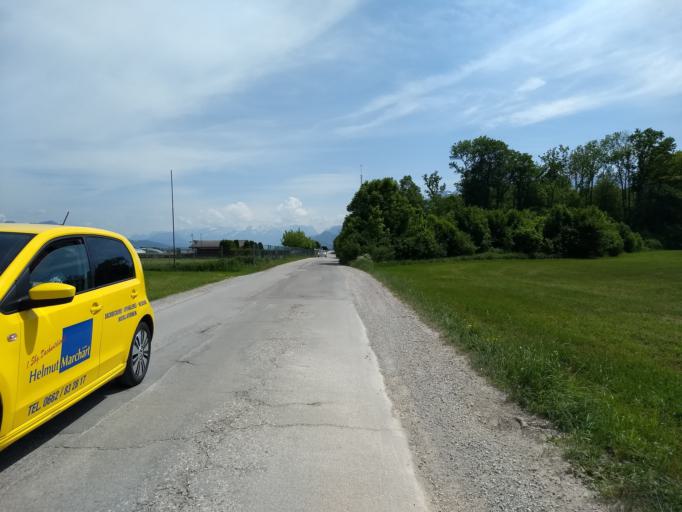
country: DE
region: Bavaria
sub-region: Upper Bavaria
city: Freilassing
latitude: 47.8039
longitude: 12.9940
